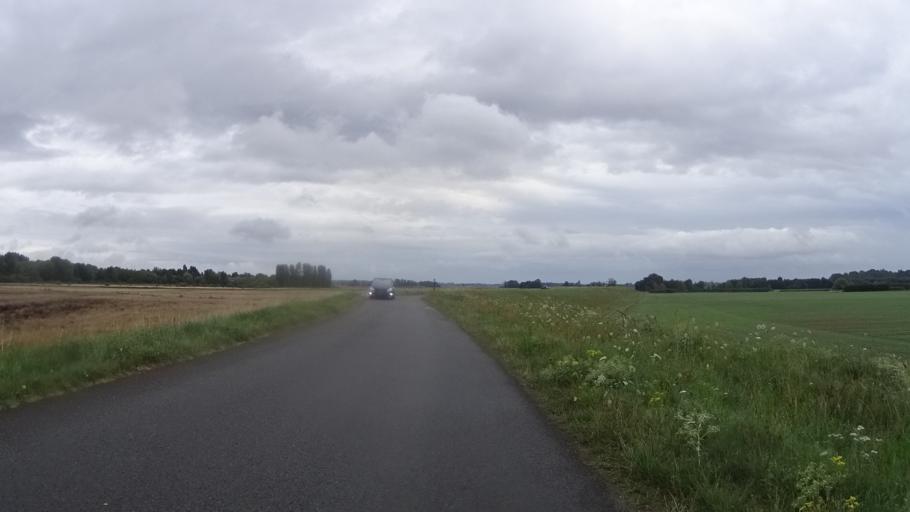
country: FR
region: Centre
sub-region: Departement du Loiret
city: Sandillon
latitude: 47.8536
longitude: 2.0520
